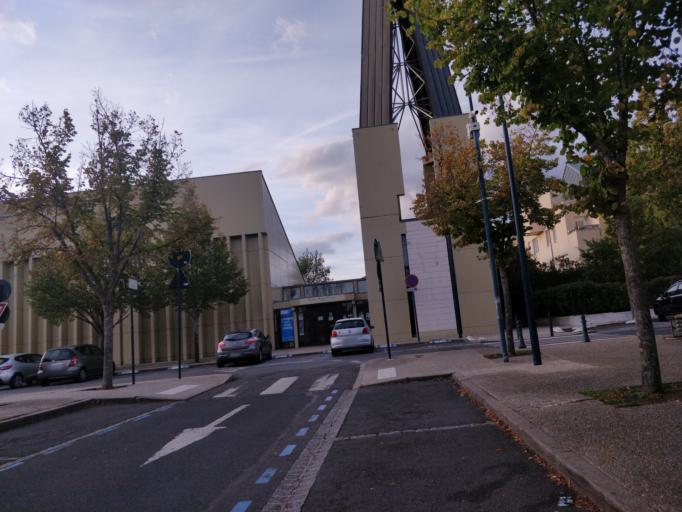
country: FR
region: Ile-de-France
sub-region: Departement du Val-d'Oise
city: Vaureal
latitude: 49.0326
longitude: 2.0192
